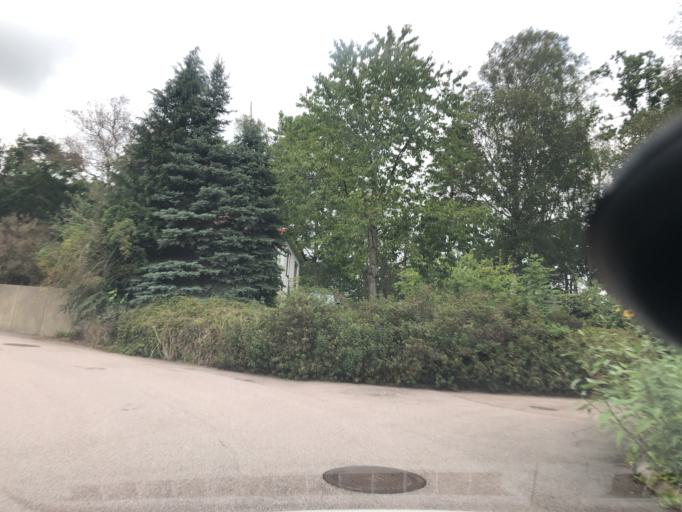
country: SE
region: Vaestra Goetaland
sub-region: Goteborg
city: Goeteborg
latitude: 57.7565
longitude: 11.9669
